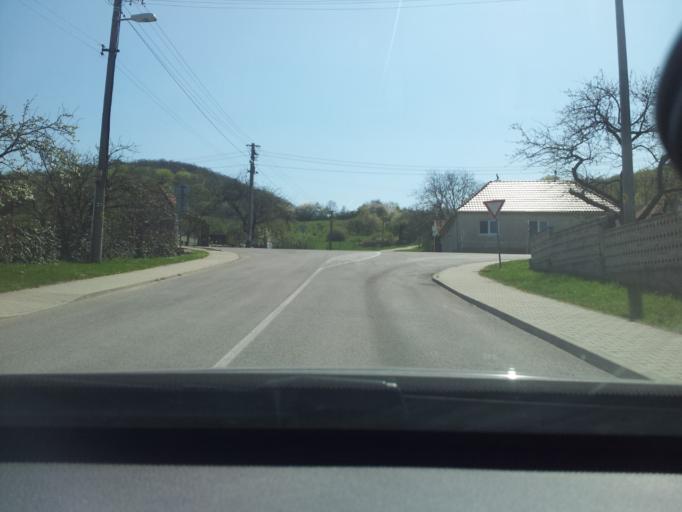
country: SK
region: Nitriansky
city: Zlate Moravce
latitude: 48.5005
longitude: 18.4263
